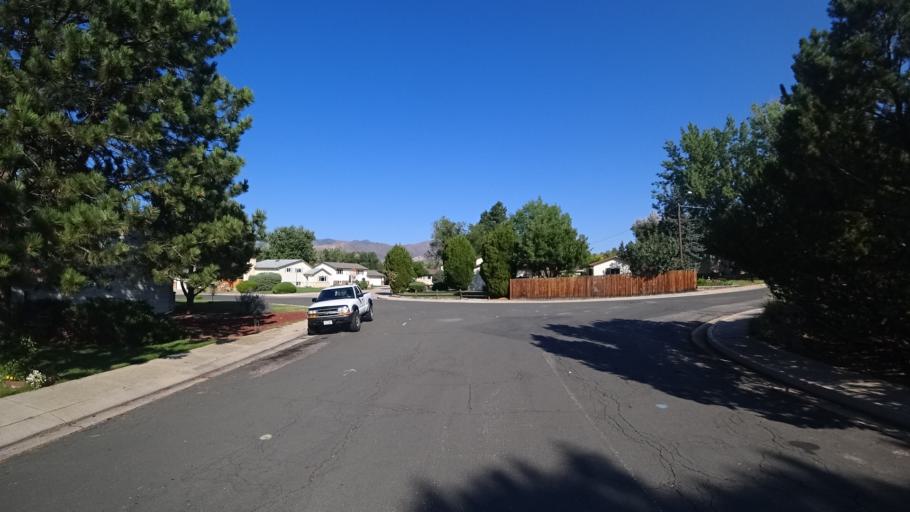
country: US
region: Colorado
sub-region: El Paso County
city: Colorado Springs
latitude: 38.8872
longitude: -104.8391
